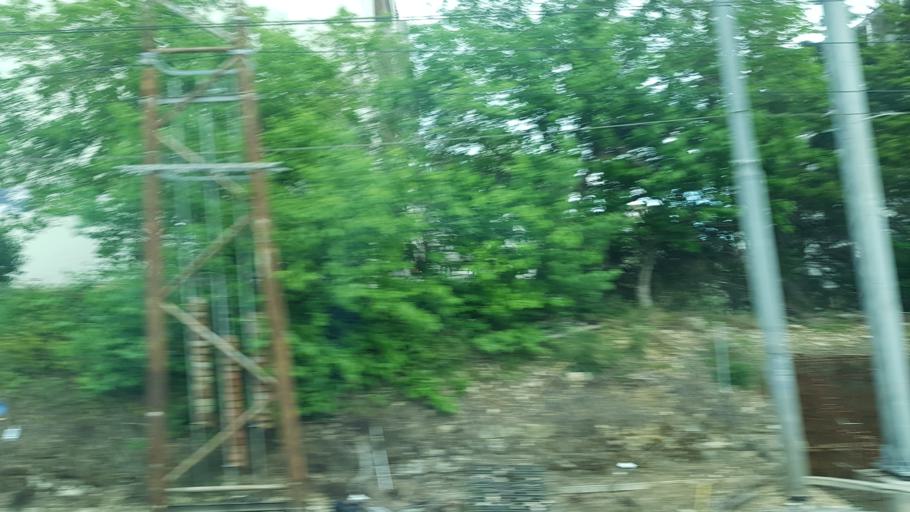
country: IT
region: Apulia
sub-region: Provincia di Brindisi
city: Brindisi
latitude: 40.6317
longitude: 17.9208
